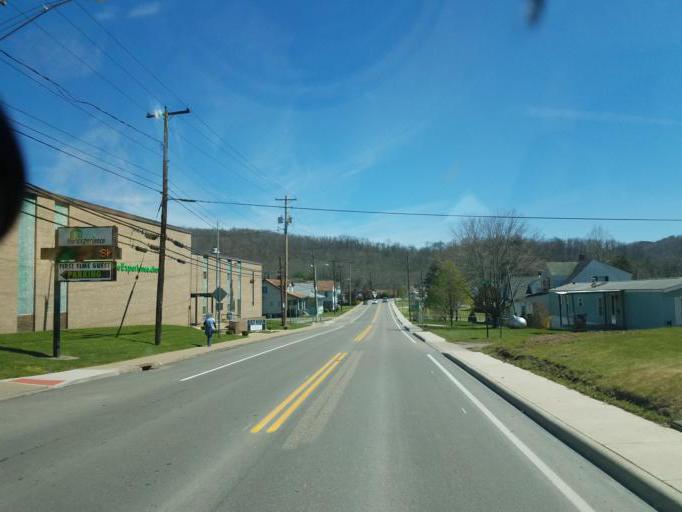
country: US
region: Ohio
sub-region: Belmont County
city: Wolfhurst
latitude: 40.0689
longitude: -80.7852
